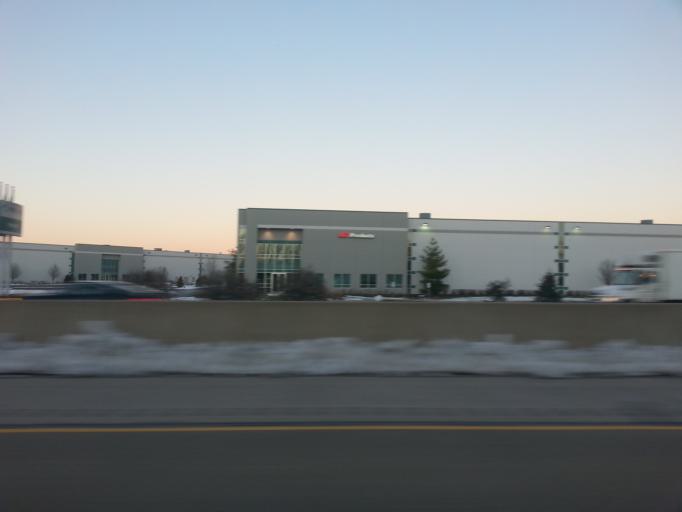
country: US
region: Illinois
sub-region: Cook County
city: Crestwood
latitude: 41.6763
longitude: -87.7725
